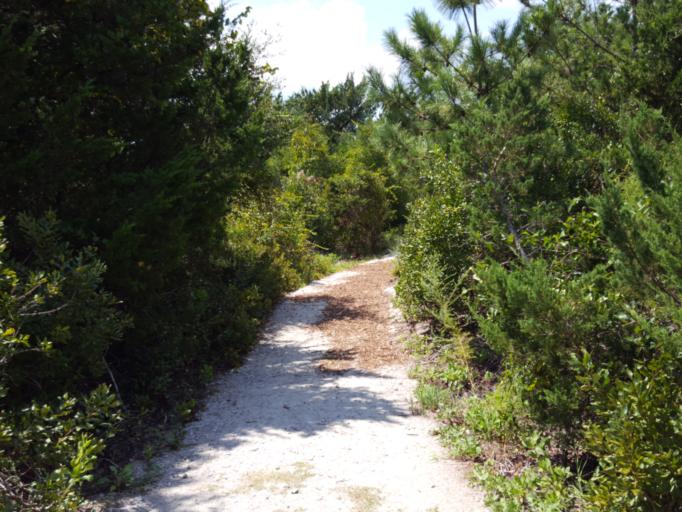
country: US
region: North Carolina
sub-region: Carteret County
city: Beaufort
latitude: 34.6951
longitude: -76.6829
